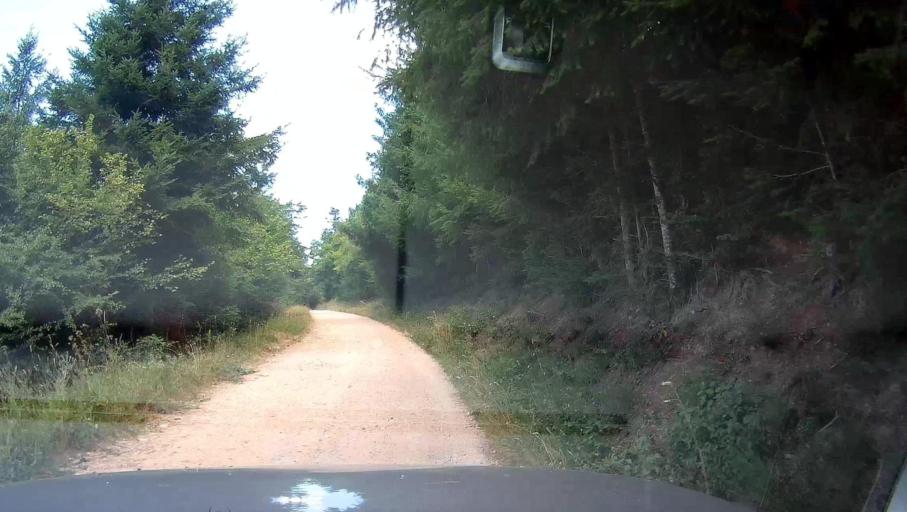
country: FR
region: Rhone-Alpes
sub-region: Departement du Rhone
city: Le Perreon
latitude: 46.0232
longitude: 4.5493
